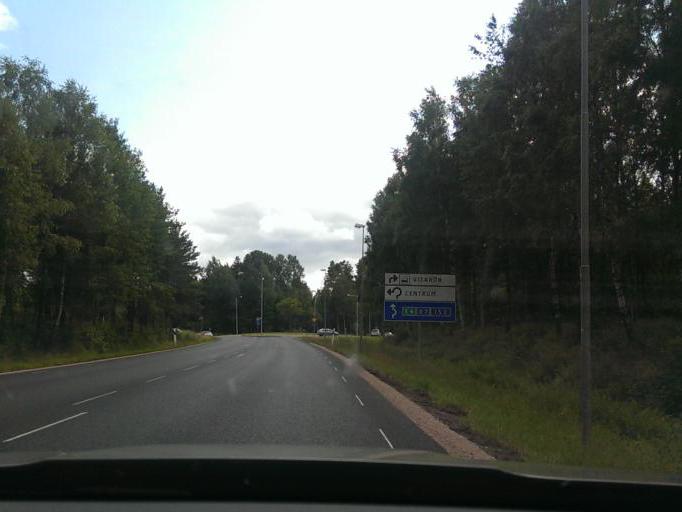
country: SE
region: Joenkoeping
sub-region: Varnamo Kommun
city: Varnamo
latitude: 57.1827
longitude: 14.0071
